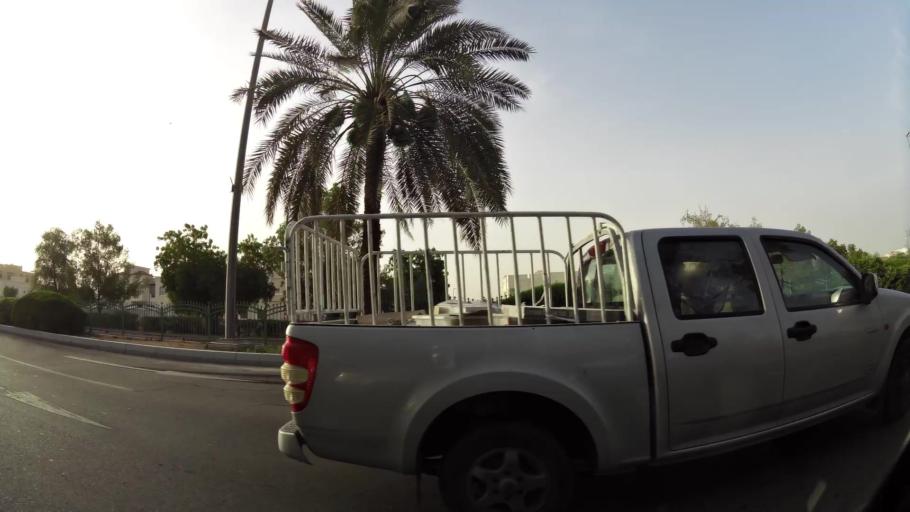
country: OM
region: Al Buraimi
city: Al Buraymi
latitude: 24.2412
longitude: 55.7424
